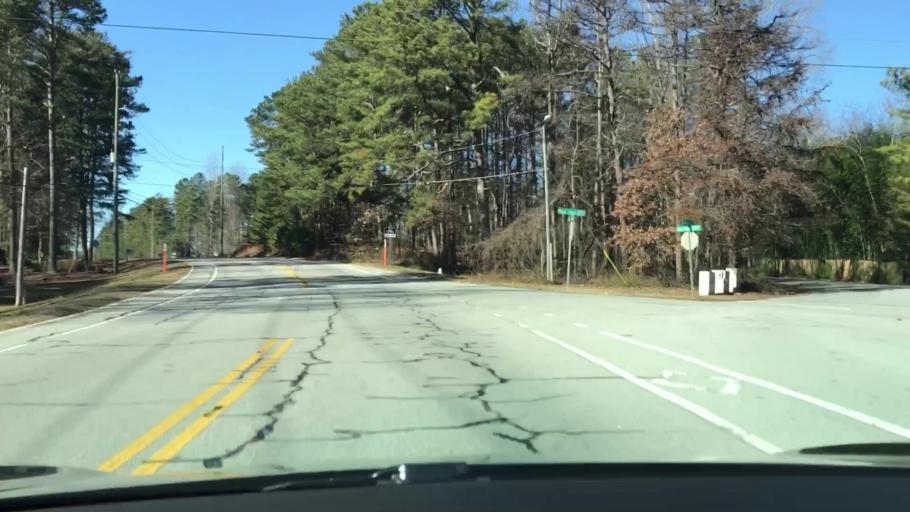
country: US
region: Georgia
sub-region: Gwinnett County
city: Buford
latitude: 34.1465
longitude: -84.0274
